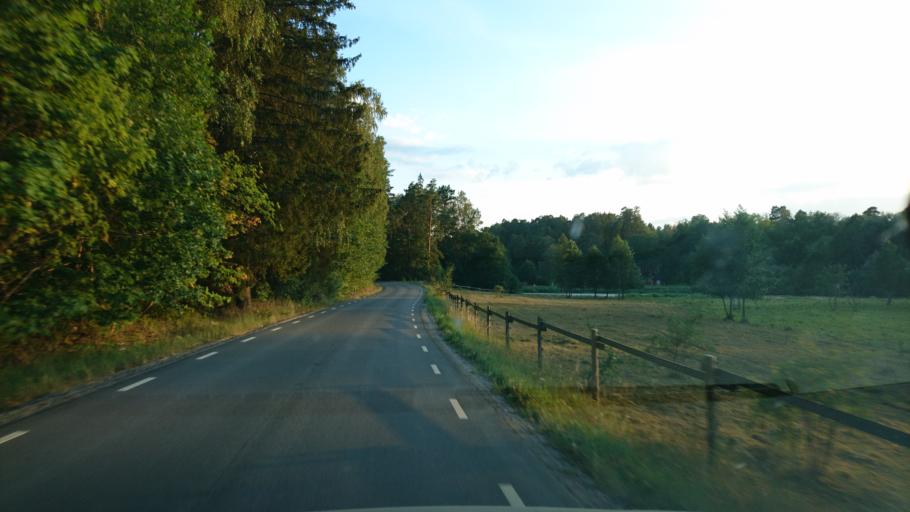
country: SE
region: Uppsala
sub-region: Uppsala Kommun
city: Saevja
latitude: 59.7909
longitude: 17.6675
